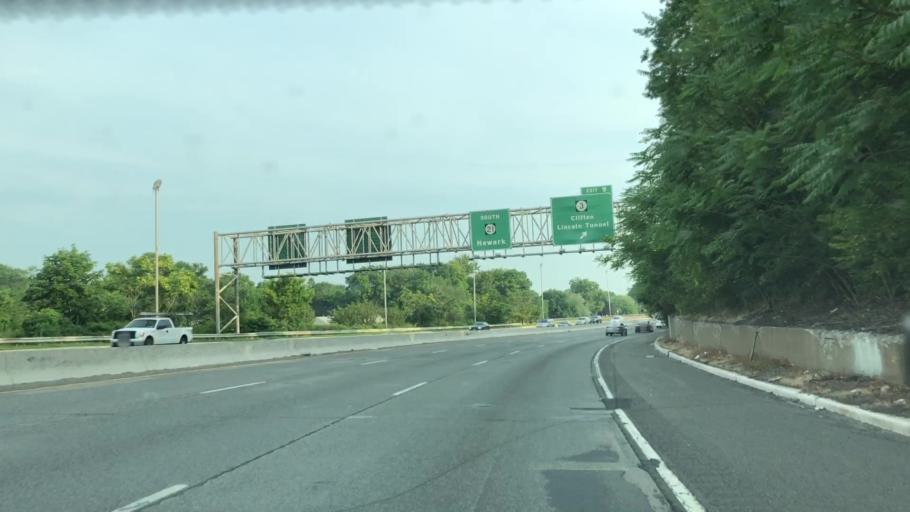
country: US
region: New Jersey
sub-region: Bergen County
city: Rutherford
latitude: 40.8308
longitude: -74.1220
